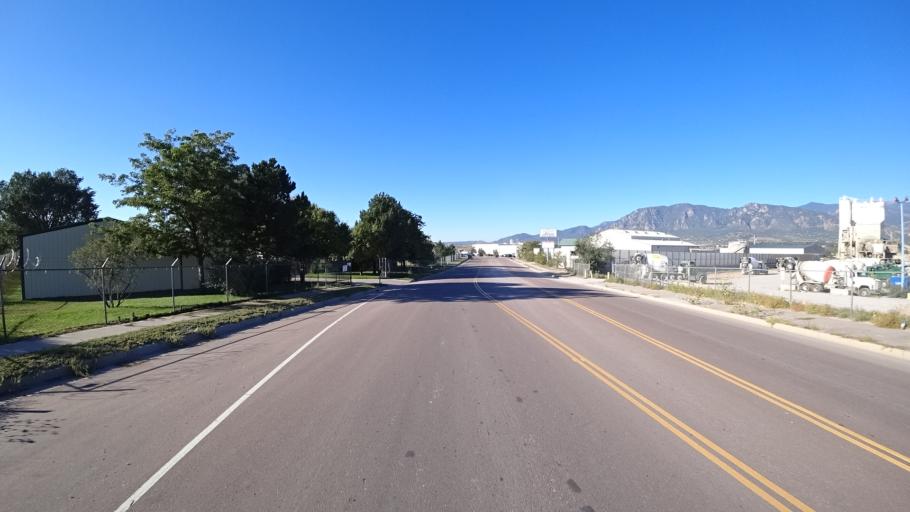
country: US
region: Colorado
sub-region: El Paso County
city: Stratmoor
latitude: 38.7872
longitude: -104.7650
